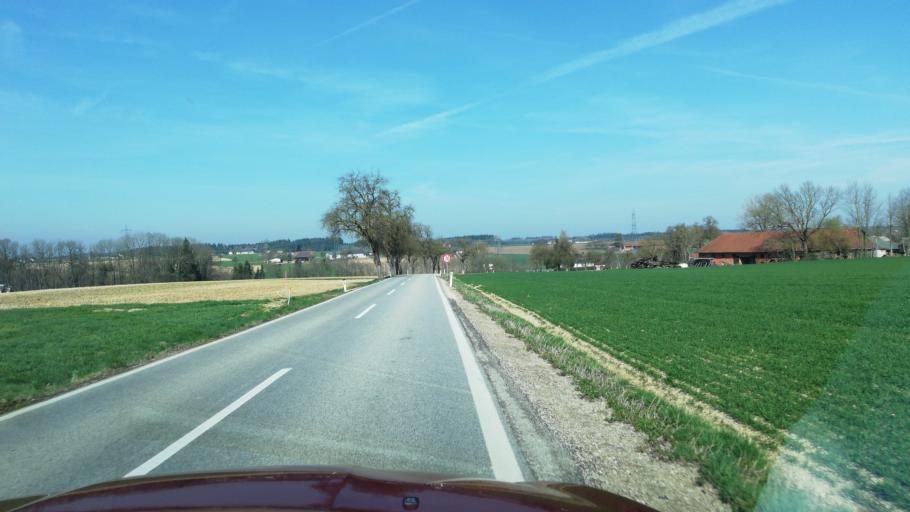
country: AT
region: Upper Austria
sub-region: Politischer Bezirk Kirchdorf an der Krems
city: Kremsmunster
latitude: 48.0861
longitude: 14.1117
